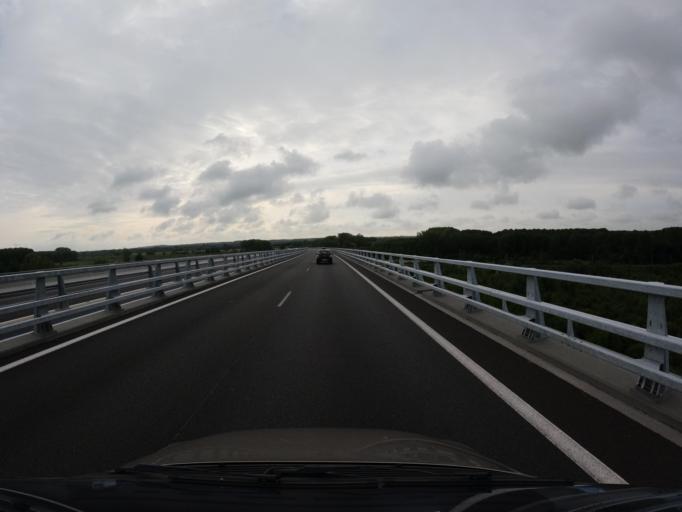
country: FR
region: Centre
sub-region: Departement d'Indre-et-Loire
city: Cinq-Mars-la-Pile
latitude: 47.3362
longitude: 0.4341
